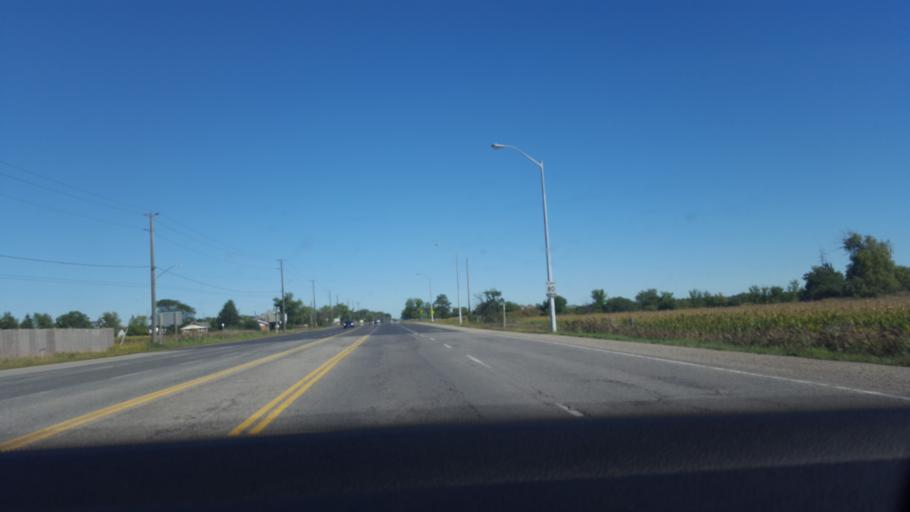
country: CA
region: Ontario
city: Hamilton
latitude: 43.1730
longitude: -79.7756
